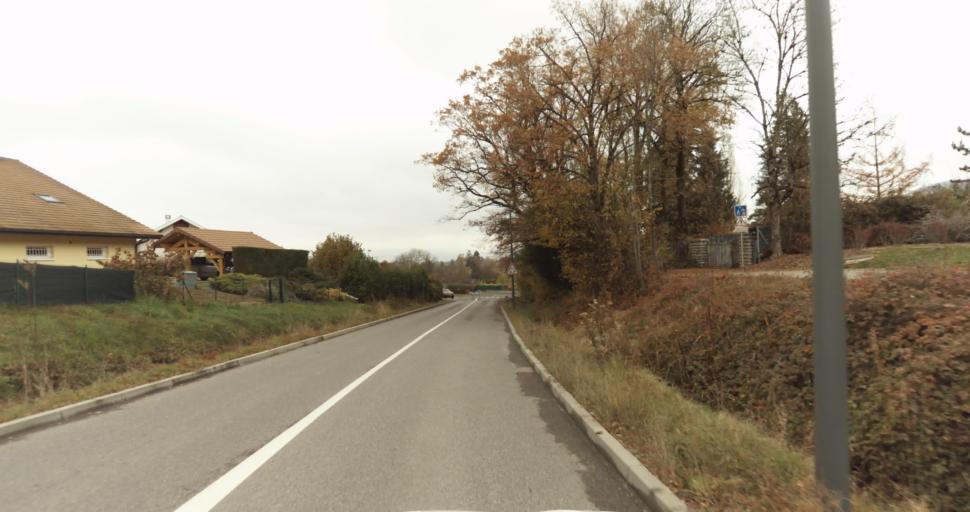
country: FR
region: Rhone-Alpes
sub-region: Departement de la Haute-Savoie
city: Seynod
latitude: 45.8565
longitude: 6.0891
